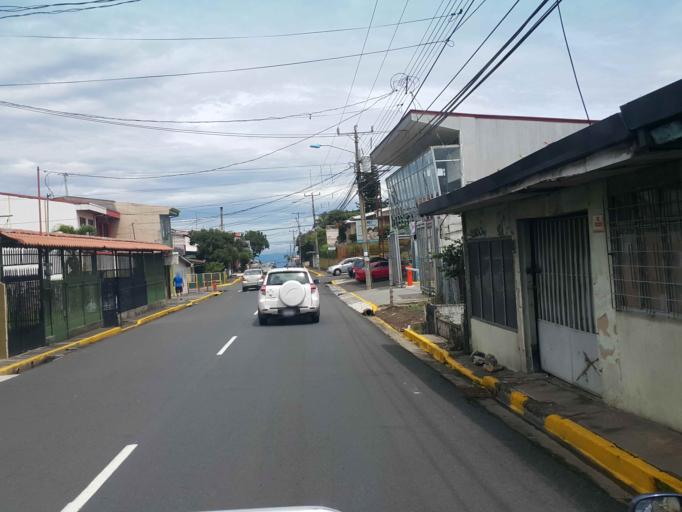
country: CR
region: Heredia
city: Heredia
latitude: 10.0045
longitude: -84.1144
